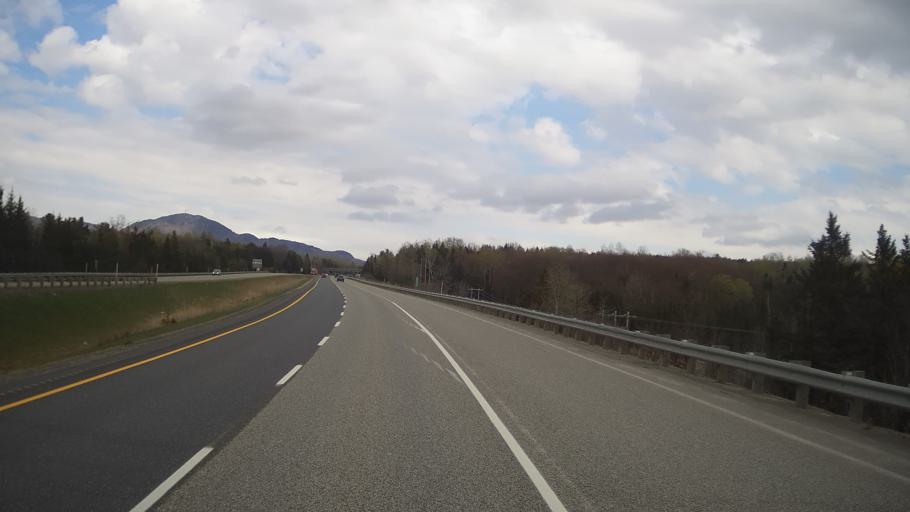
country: CA
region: Quebec
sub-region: Estrie
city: Magog
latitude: 45.2974
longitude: -72.3138
